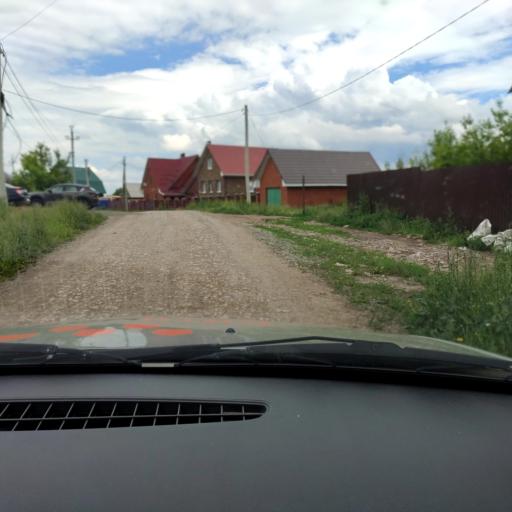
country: RU
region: Bashkortostan
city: Ufa
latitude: 54.6004
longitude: 55.9252
